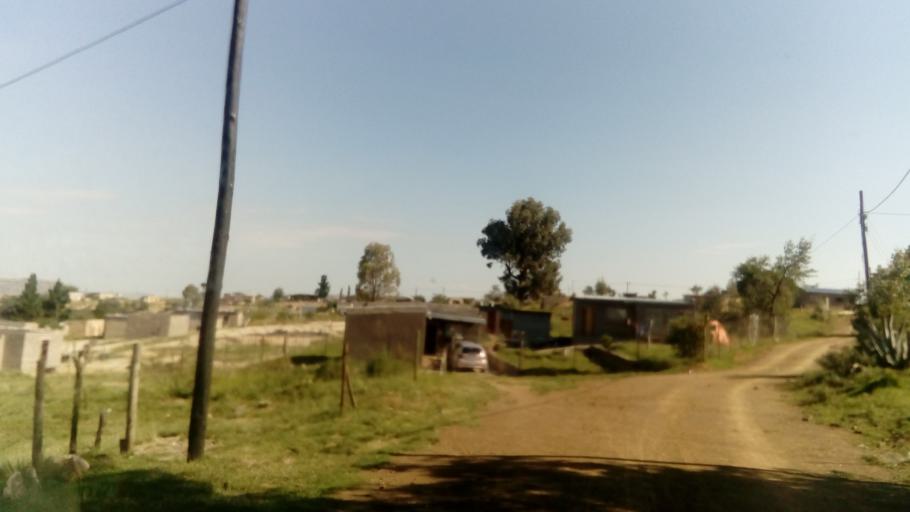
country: LS
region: Berea
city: Teyateyaneng
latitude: -29.1393
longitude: 27.7484
